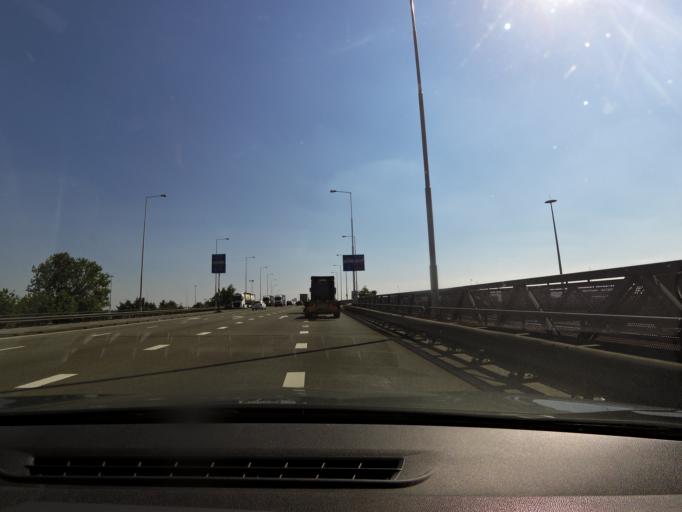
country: NL
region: South Holland
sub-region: Gemeente Albrandswaard
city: Rhoon
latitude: 51.8736
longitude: 4.4301
